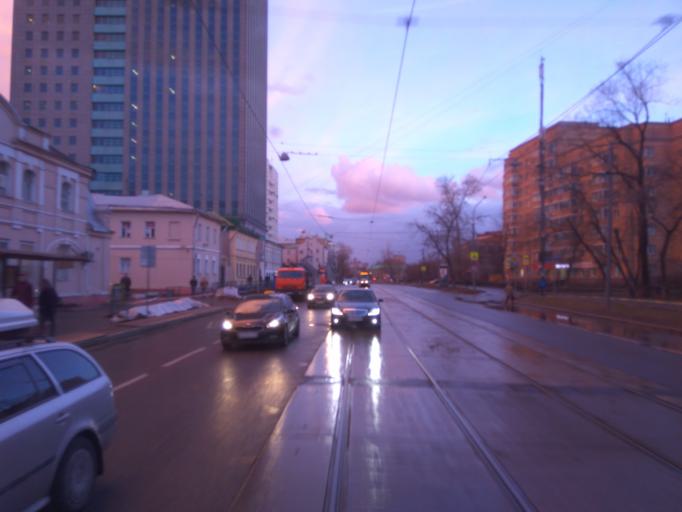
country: RU
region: Moscow
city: Zamoskvorech'ye
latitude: 55.7262
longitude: 37.6373
